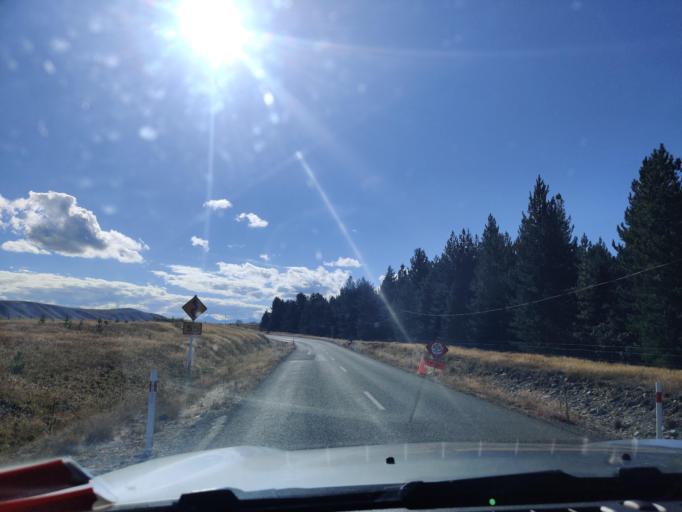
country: NZ
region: Canterbury
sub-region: Timaru District
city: Pleasant Point
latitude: -44.0016
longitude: 170.4541
